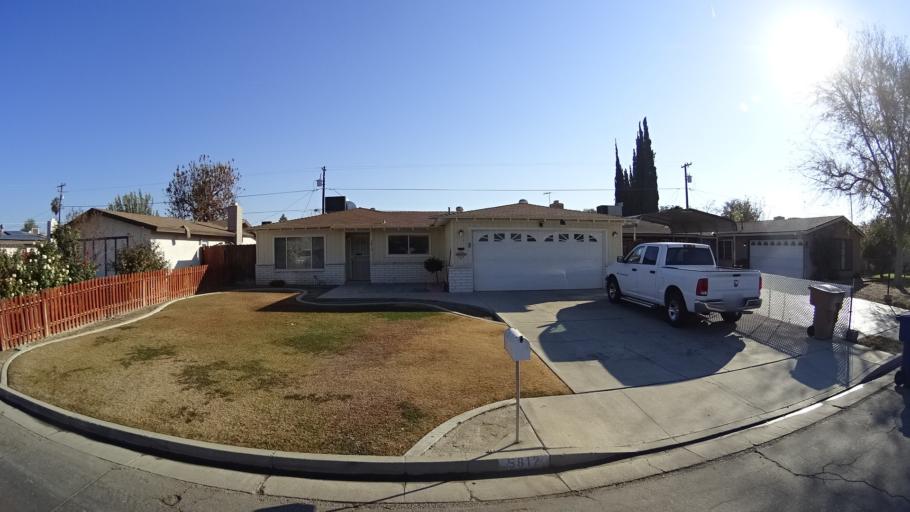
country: US
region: California
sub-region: Kern County
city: Greenfield
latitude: 35.3015
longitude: -119.0177
